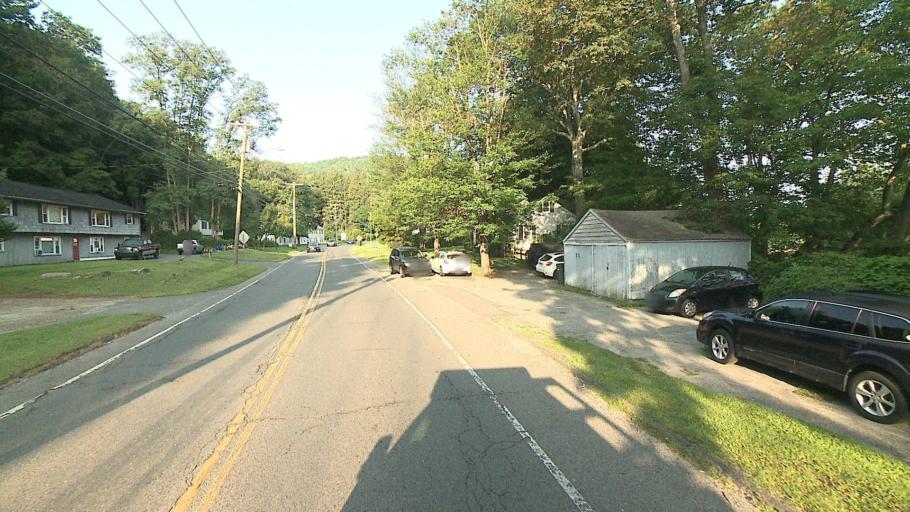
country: US
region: Connecticut
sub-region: Litchfield County
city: New Milford
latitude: 41.5828
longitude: -73.4375
